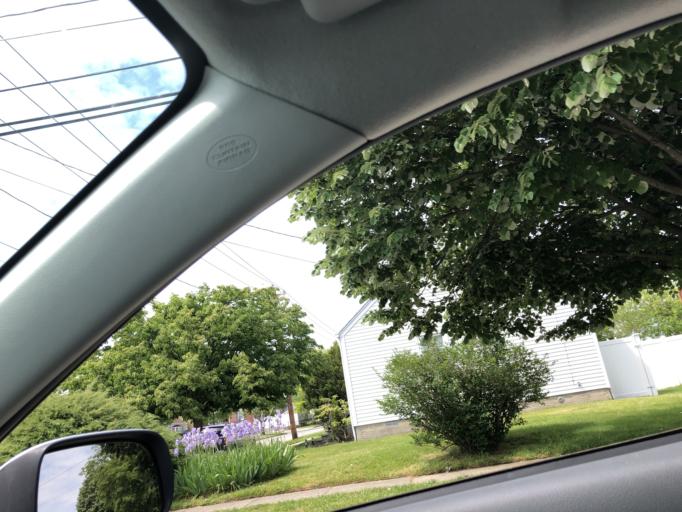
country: US
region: New York
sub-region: Nassau County
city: Oceanside
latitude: 40.6358
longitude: -73.6492
